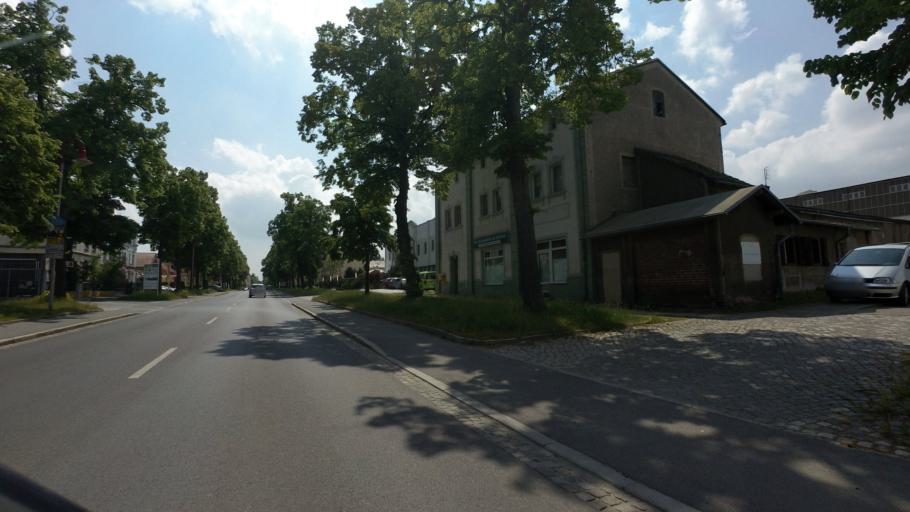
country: DE
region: Saxony
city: Niesky
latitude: 51.2976
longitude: 14.8250
